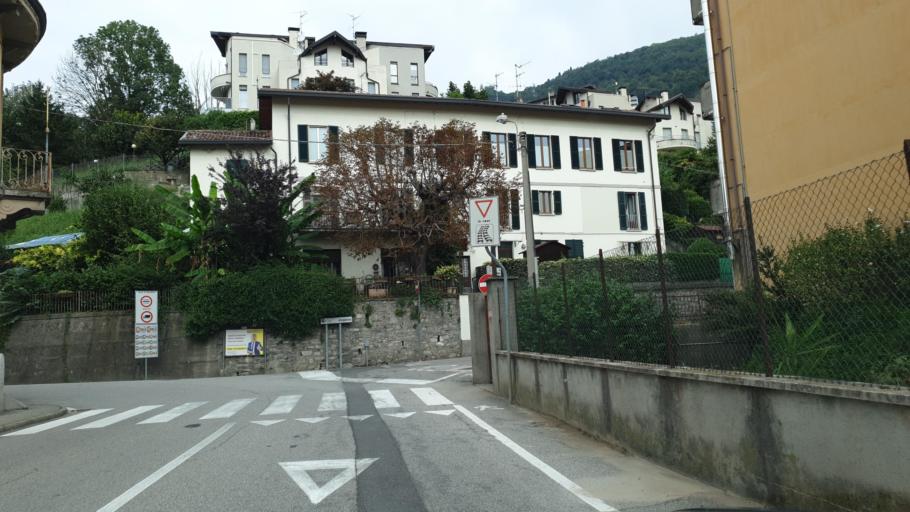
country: IT
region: Lombardy
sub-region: Provincia di Como
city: Maslianico
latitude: 45.8437
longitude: 9.0394
